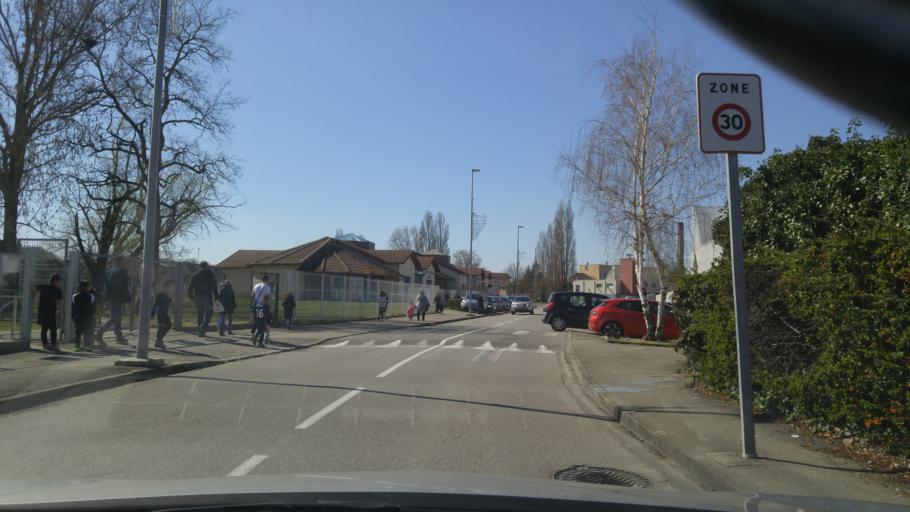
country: FR
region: Rhone-Alpes
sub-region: Departement de l'Isere
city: Pont-de-Cheruy
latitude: 45.7492
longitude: 5.1710
